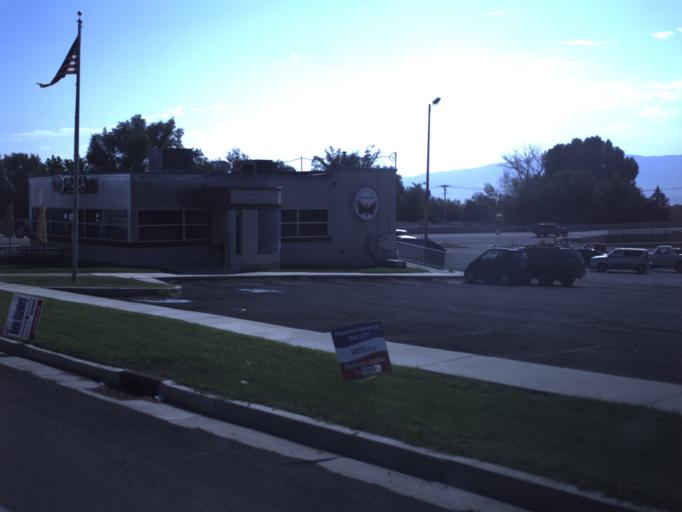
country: US
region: Utah
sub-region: Utah County
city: Pleasant Grove
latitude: 40.3601
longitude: -111.7408
